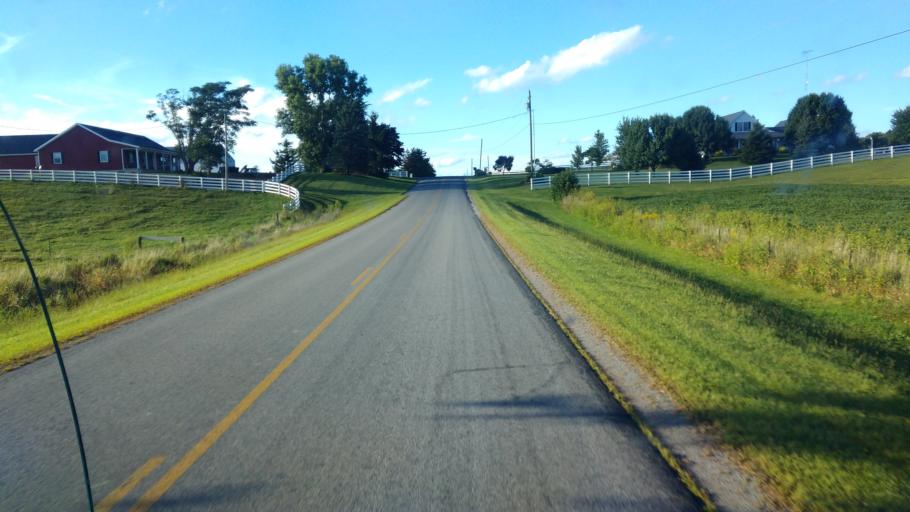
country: US
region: Ohio
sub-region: Wyandot County
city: Upper Sandusky
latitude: 40.8372
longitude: -83.3808
